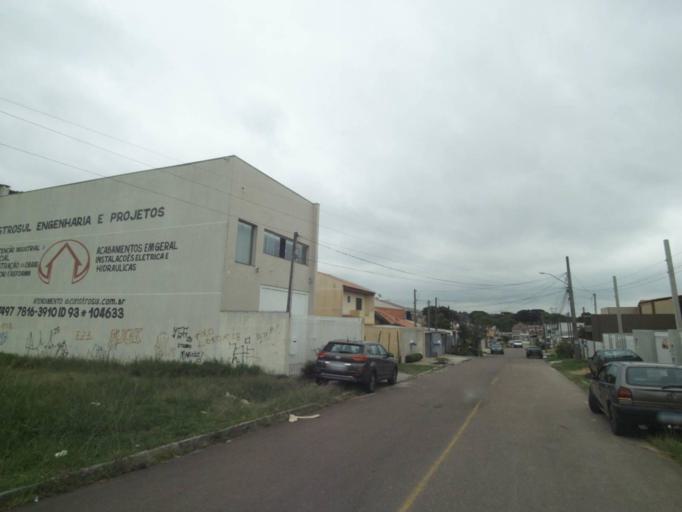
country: BR
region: Parana
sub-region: Araucaria
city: Araucaria
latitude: -25.5425
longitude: -49.3375
